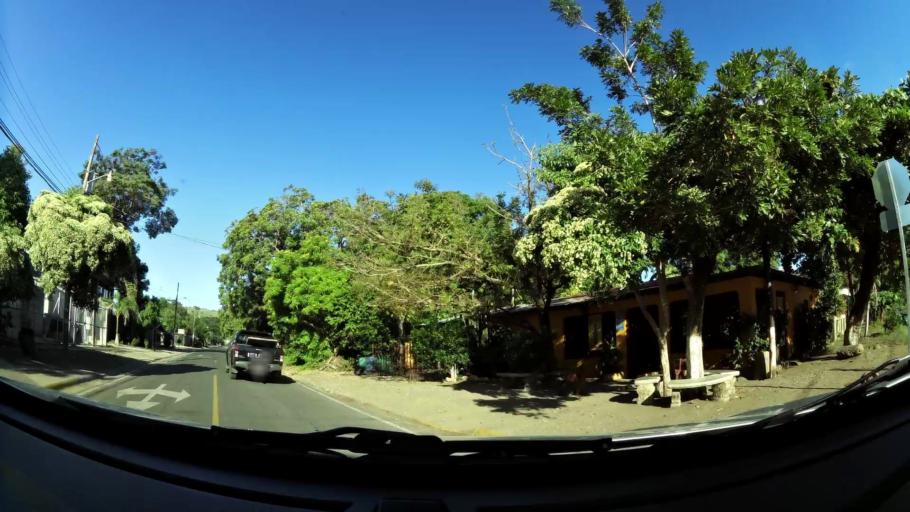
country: CR
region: Guanacaste
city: Sardinal
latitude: 10.5177
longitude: -85.6472
